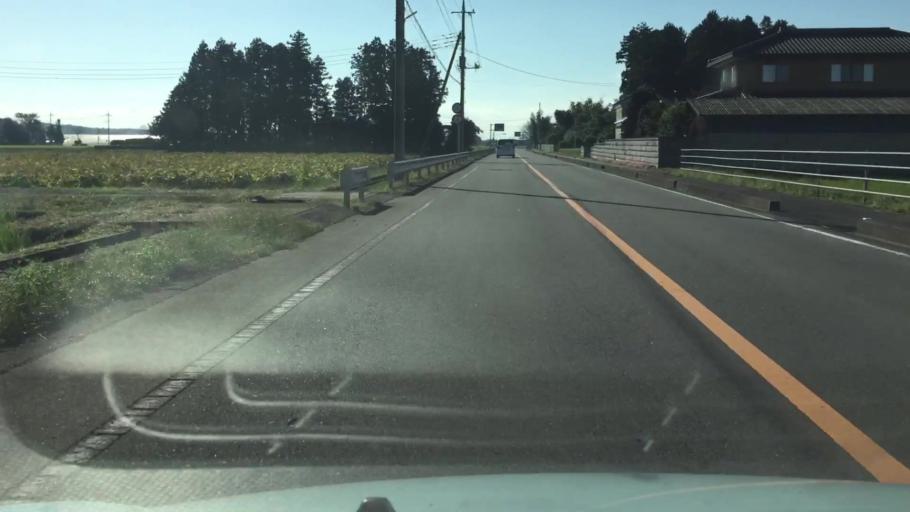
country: JP
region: Tochigi
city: Ujiie
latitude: 36.6786
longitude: 140.0114
